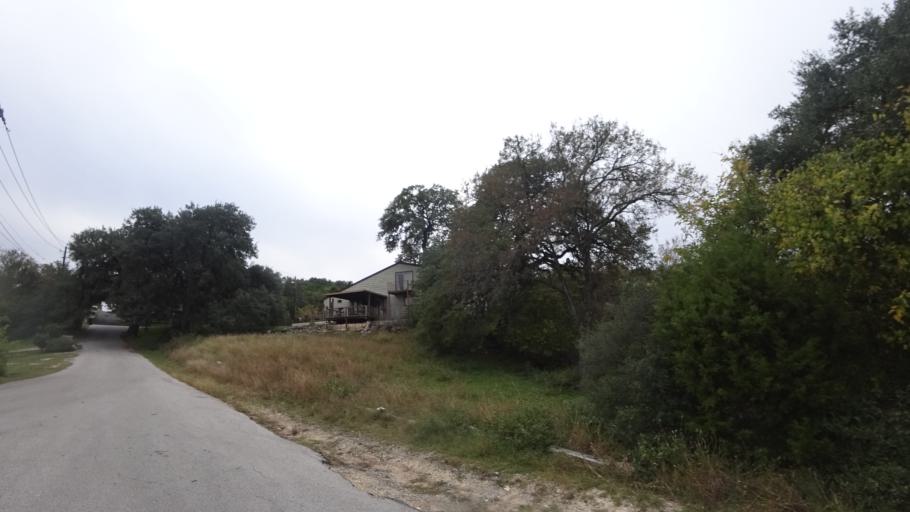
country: US
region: Texas
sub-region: Travis County
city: Hudson Bend
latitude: 30.3762
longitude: -97.9160
